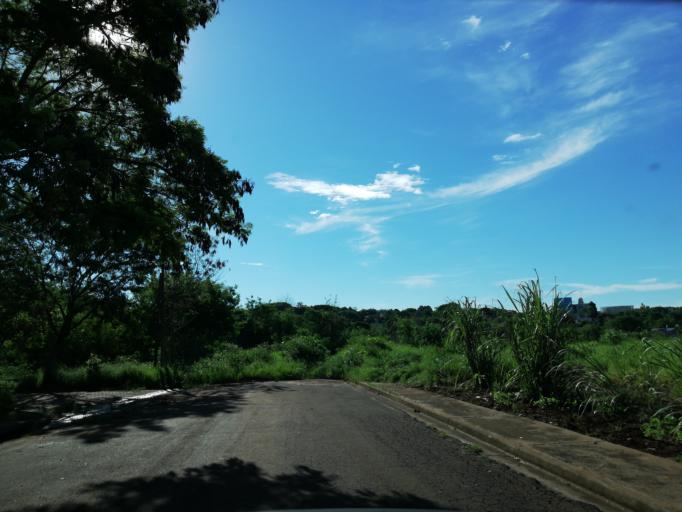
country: AR
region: Misiones
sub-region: Departamento de Capital
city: Posadas
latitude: -27.4030
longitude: -55.9569
